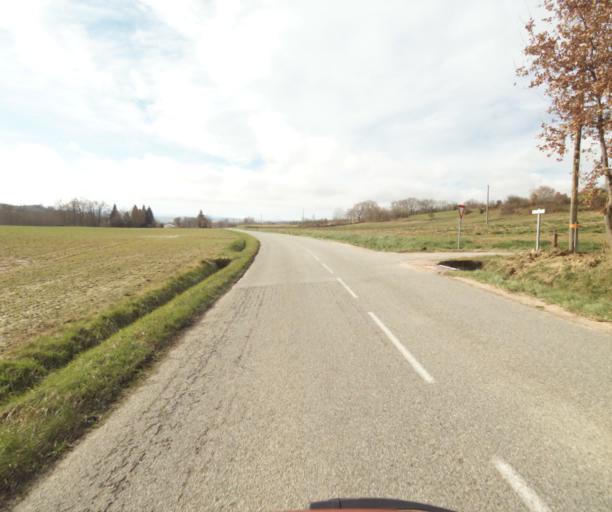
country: FR
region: Midi-Pyrenees
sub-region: Departement de l'Ariege
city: Pamiers
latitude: 43.1389
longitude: 1.5630
